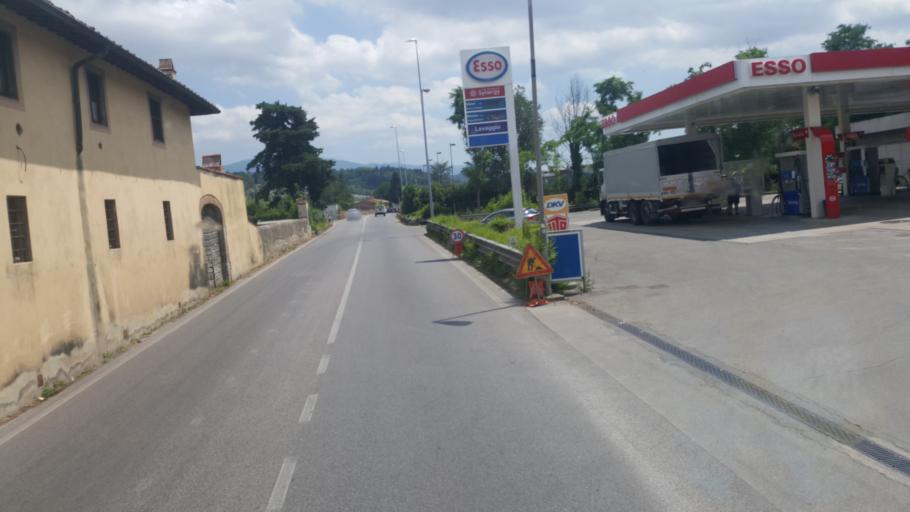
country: IT
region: Tuscany
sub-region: Province of Florence
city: Sieci
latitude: 43.7851
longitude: 11.4009
